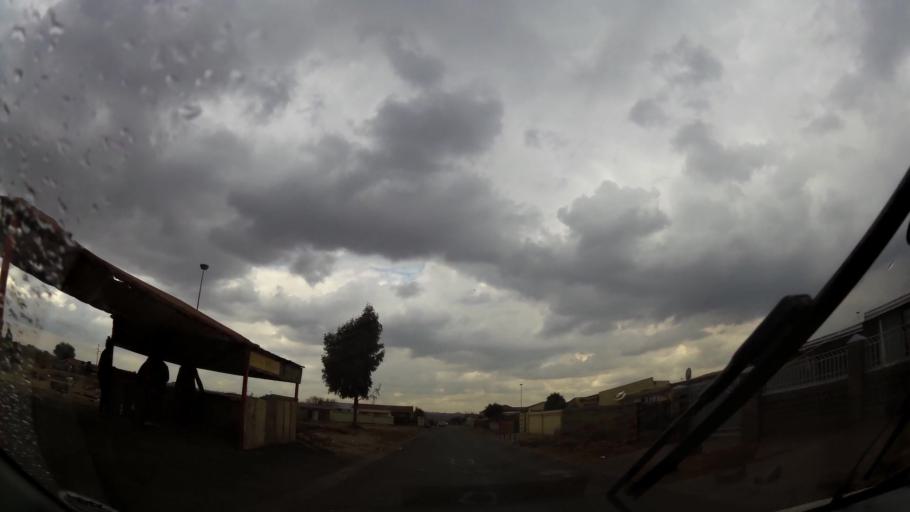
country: ZA
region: Gauteng
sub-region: Ekurhuleni Metropolitan Municipality
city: Germiston
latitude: -26.3606
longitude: 28.1629
